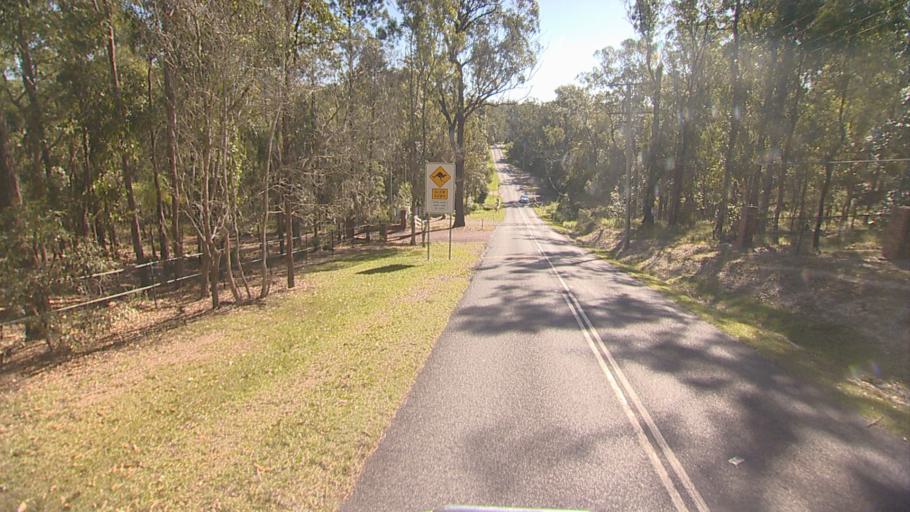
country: AU
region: Queensland
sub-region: Logan
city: Springwood
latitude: -27.6023
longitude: 153.1697
